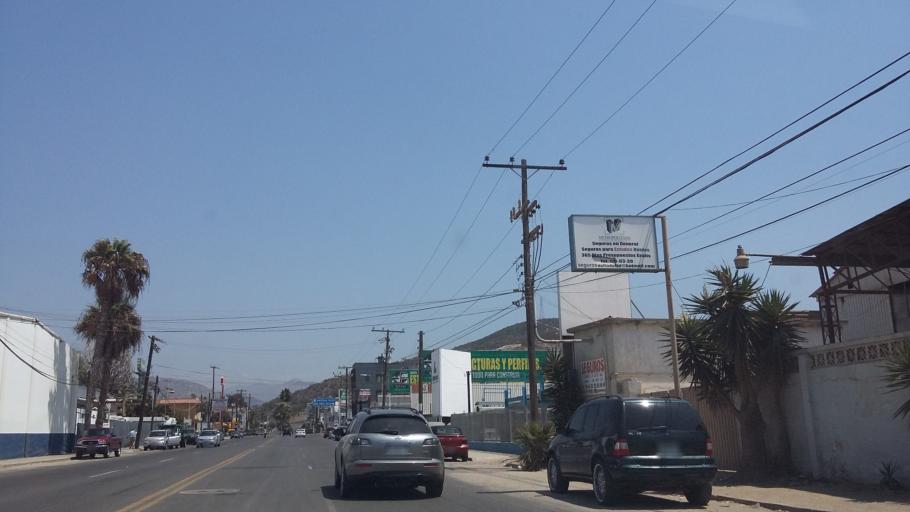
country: MX
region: Baja California
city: Ensenada
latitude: 31.8413
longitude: -116.6055
